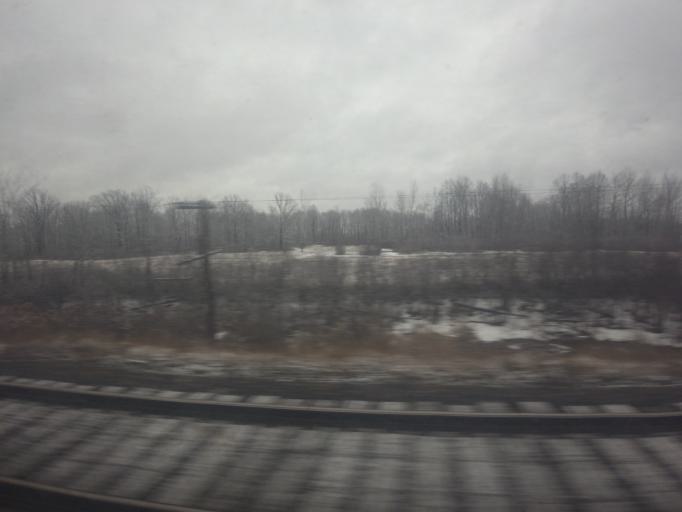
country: US
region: New York
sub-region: Jefferson County
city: Alexandria Bay
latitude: 44.4121
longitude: -76.0031
